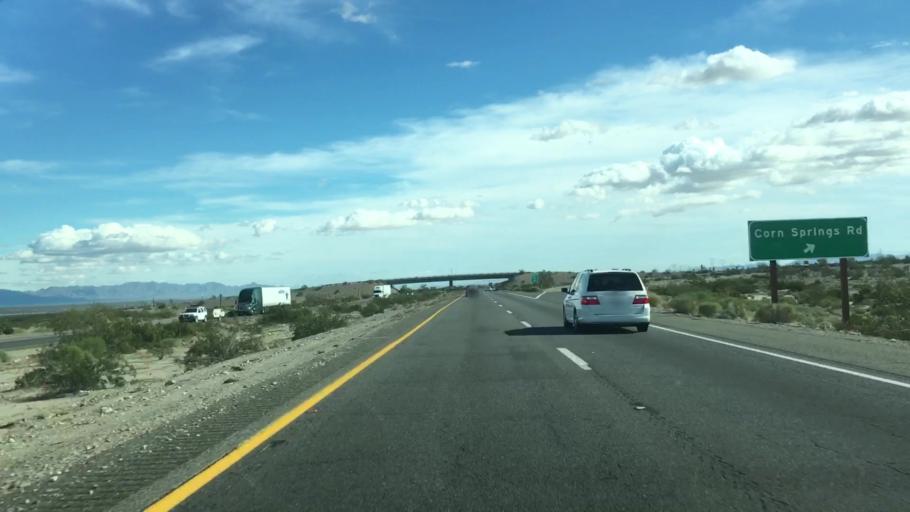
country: US
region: California
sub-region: Imperial County
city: Niland
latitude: 33.6836
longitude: -115.2475
